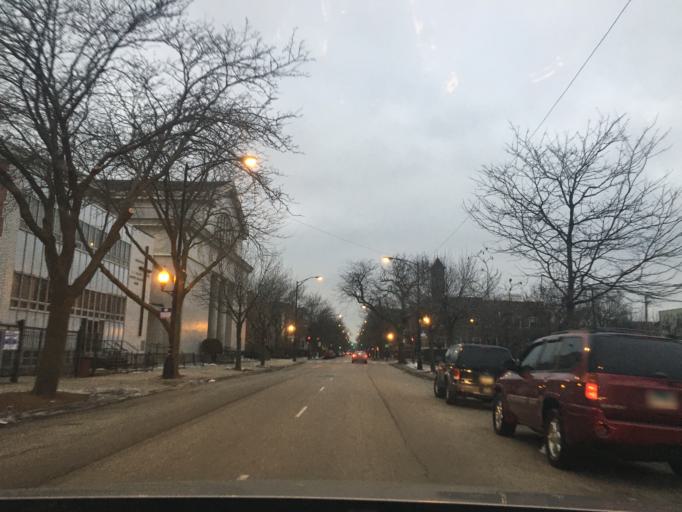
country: US
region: Illinois
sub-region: Cook County
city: Chicago
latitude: 41.8831
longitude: -87.6805
